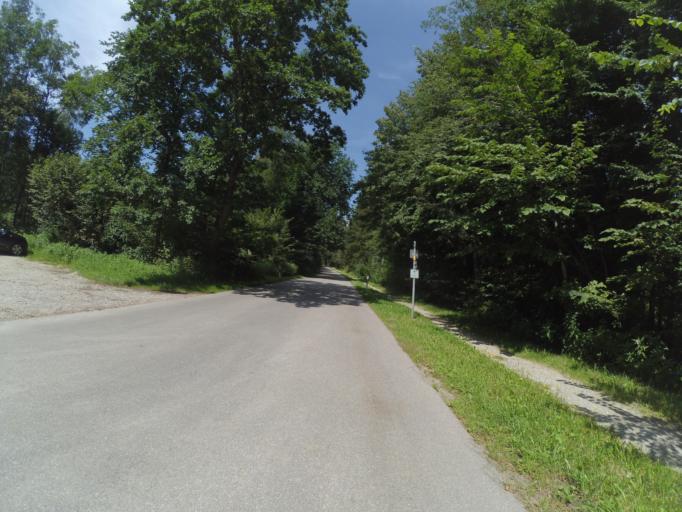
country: DE
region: Bavaria
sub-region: Swabia
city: Baisweil
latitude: 47.9814
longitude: 10.5695
